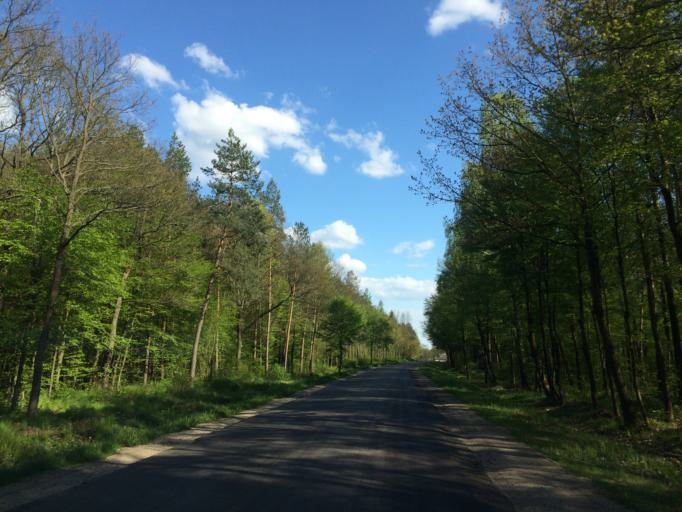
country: PL
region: Warmian-Masurian Voivodeship
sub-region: Powiat dzialdowski
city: Rybno
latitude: 53.3611
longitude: 19.9452
